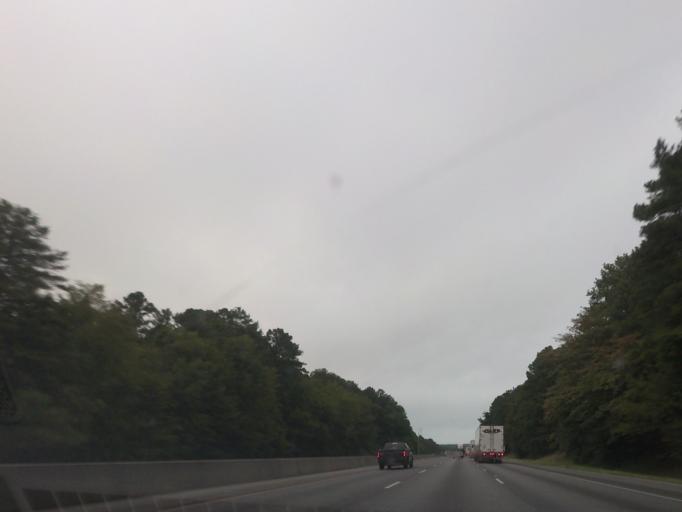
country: US
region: Georgia
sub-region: Bibb County
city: West Point
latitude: 32.8428
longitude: -83.7377
